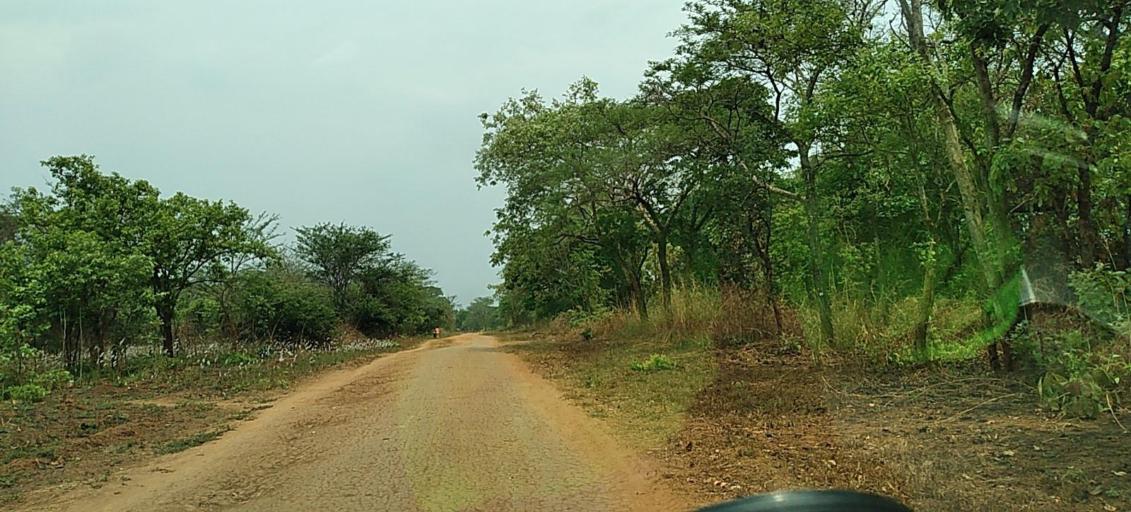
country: ZM
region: North-Western
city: Solwezi
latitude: -12.7973
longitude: 26.5336
